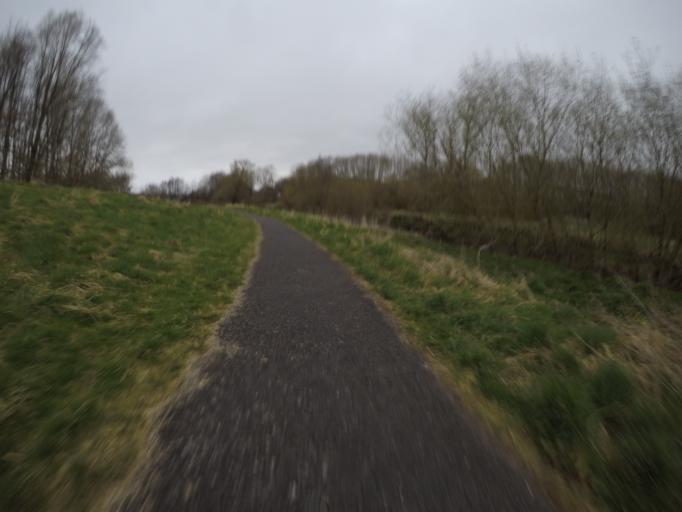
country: GB
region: Scotland
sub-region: North Ayrshire
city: Irvine
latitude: 55.6111
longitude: -4.6384
